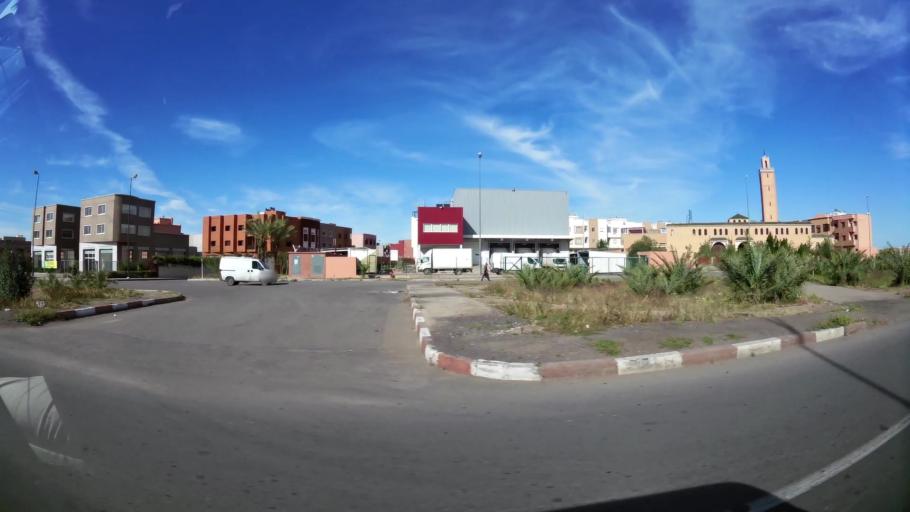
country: MA
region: Marrakech-Tensift-Al Haouz
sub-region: Marrakech
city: Marrakesh
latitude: 31.6791
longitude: -8.0478
